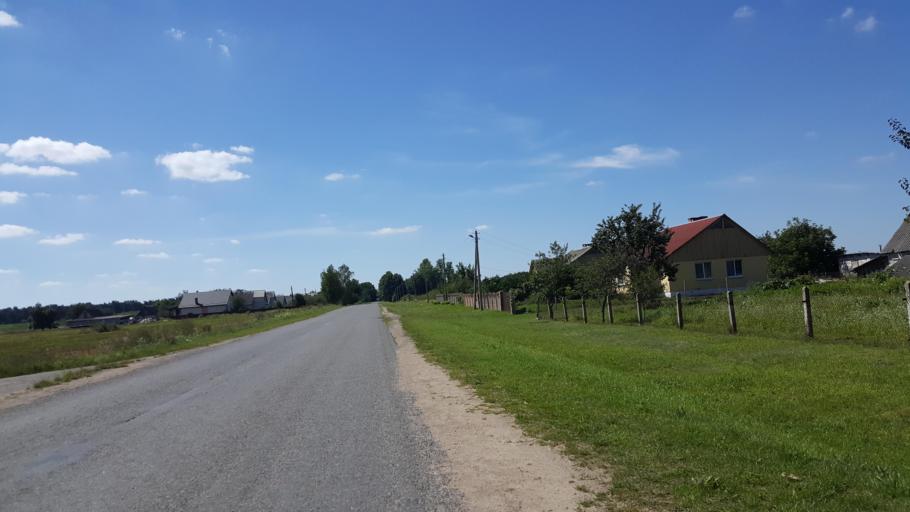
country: BY
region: Brest
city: Charnawchytsy
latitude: 52.3655
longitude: 23.6251
